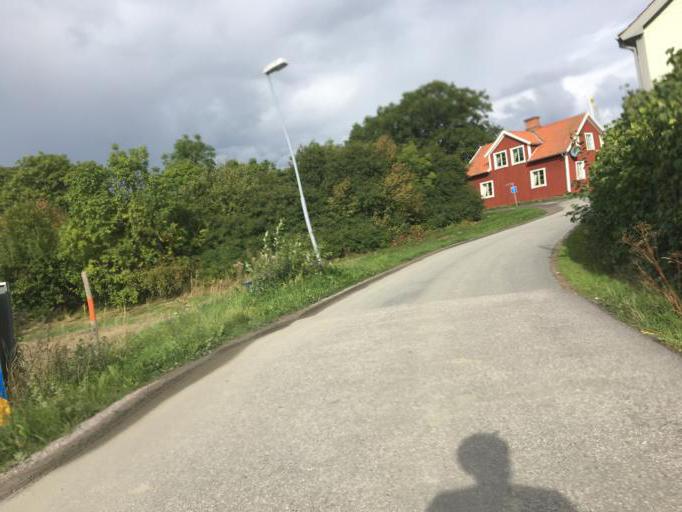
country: SE
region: Soedermanland
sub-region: Eskilstuna Kommun
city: Eskilstuna
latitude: 59.4479
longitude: 16.6427
